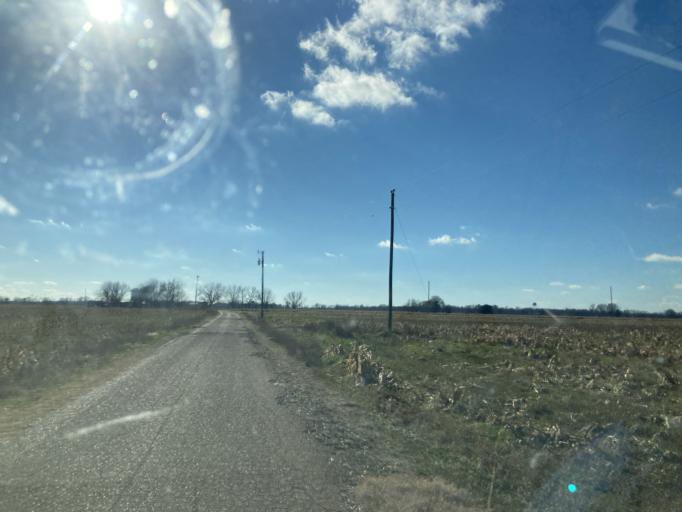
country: US
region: Mississippi
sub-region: Yazoo County
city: Yazoo City
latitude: 32.9272
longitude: -90.4722
